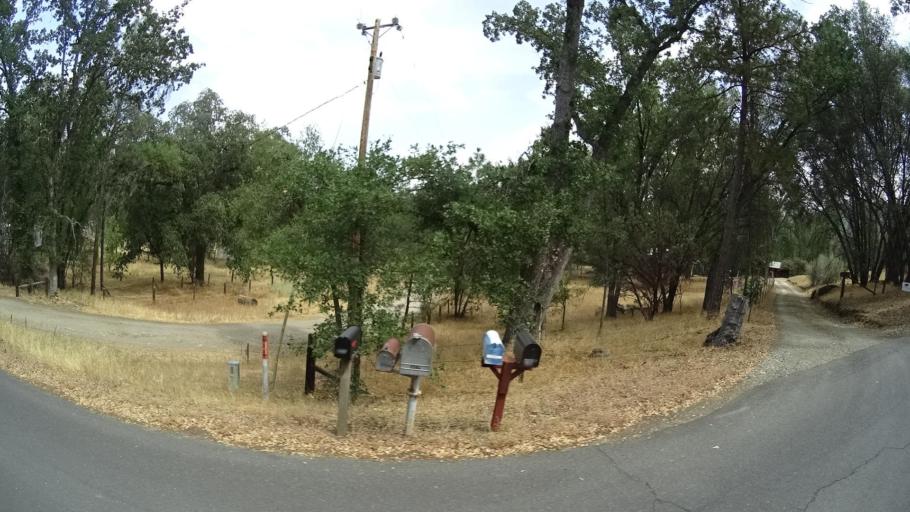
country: US
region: California
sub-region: Mariposa County
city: Midpines
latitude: 37.4499
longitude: -119.8463
